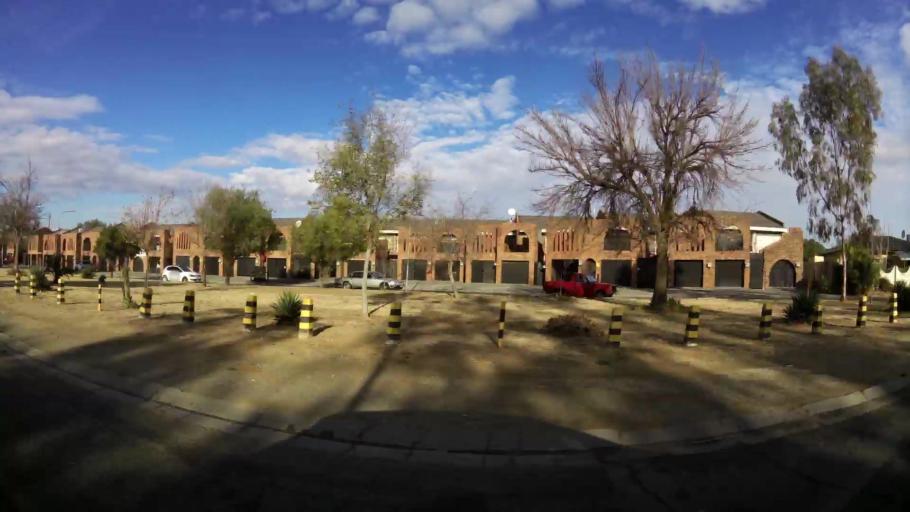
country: ZA
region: Orange Free State
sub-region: Lejweleputswa District Municipality
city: Welkom
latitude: -27.9904
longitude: 26.7519
